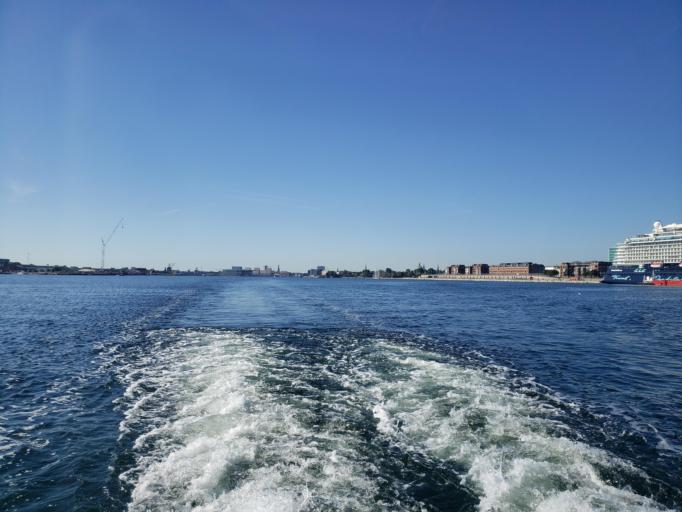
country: DK
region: Capital Region
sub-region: Kobenhavn
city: Christianshavn
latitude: 55.7029
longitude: 12.6073
